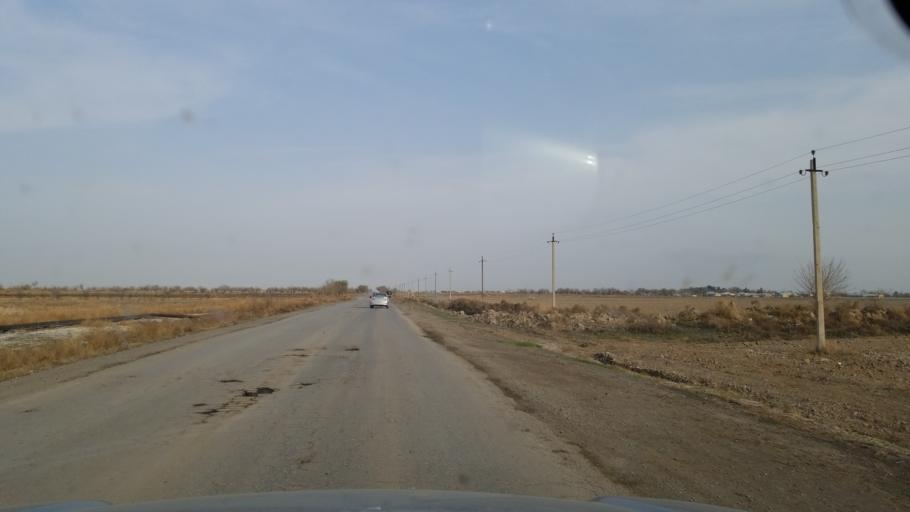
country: TM
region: Mary
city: Bayramaly
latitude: 37.6121
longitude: 62.2440
